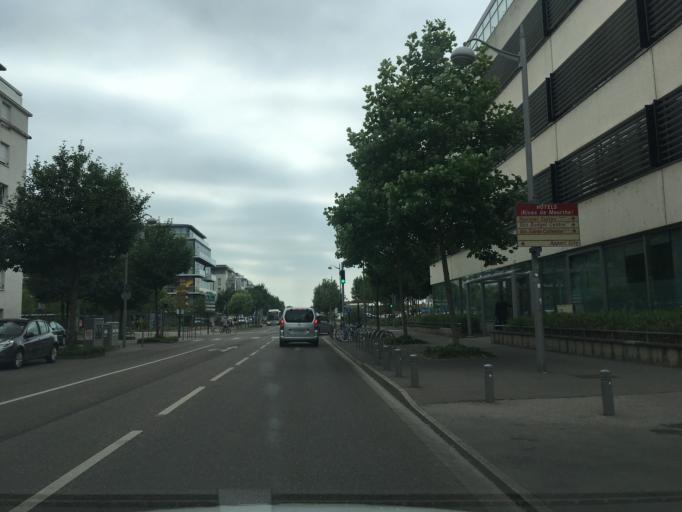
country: FR
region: Lorraine
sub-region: Departement de Meurthe-et-Moselle
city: Nancy
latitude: 48.6934
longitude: 6.1961
